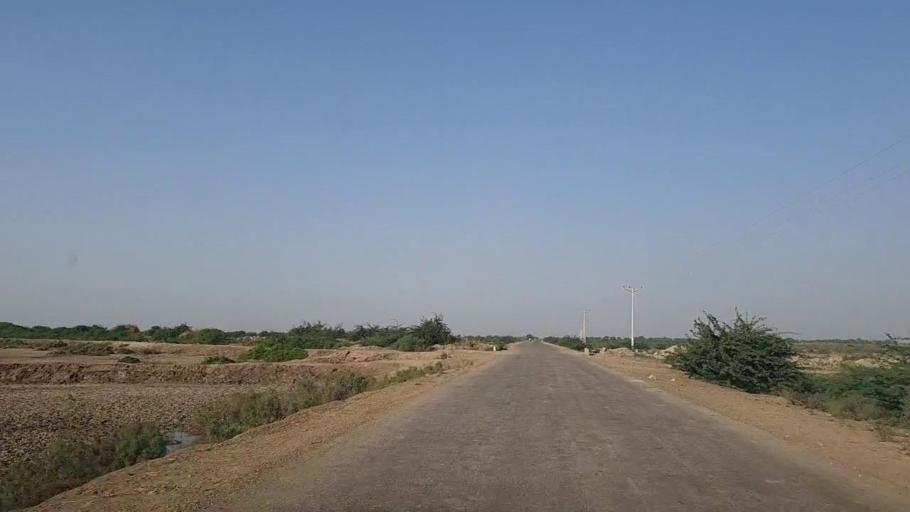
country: PK
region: Sindh
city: Mirpur Batoro
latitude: 24.6133
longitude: 68.4041
